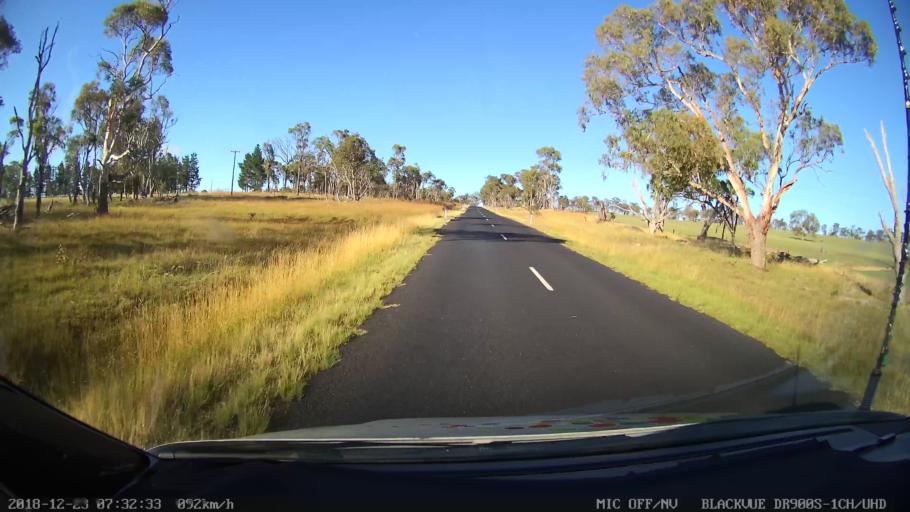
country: AU
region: New South Wales
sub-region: Armidale Dumaresq
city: Enmore
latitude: -30.5055
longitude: 152.1153
